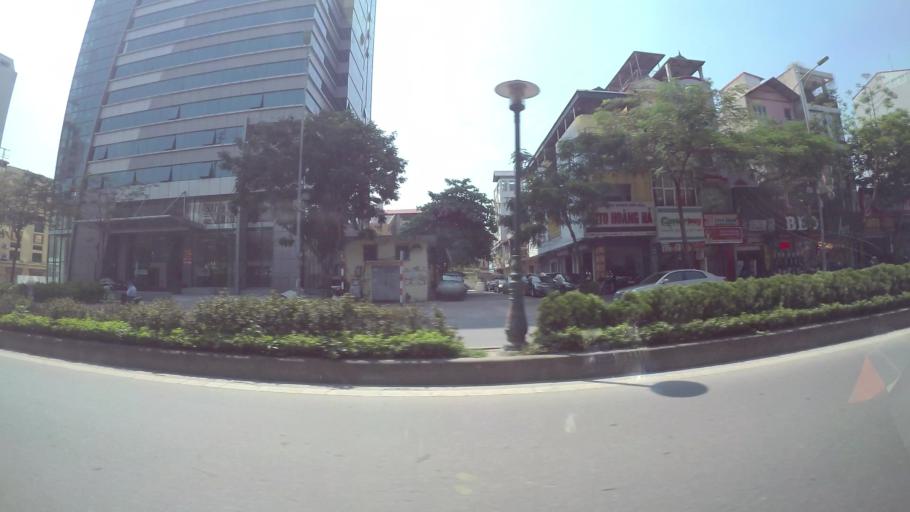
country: VN
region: Ha Noi
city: Hoan Kiem
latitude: 21.0481
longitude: 105.8815
